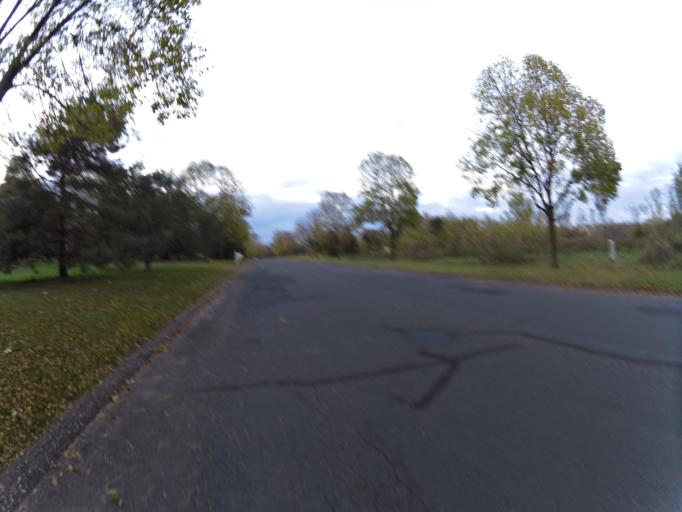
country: US
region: Minnesota
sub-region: Washington County
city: Lakeland
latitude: 44.9591
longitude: -92.8218
